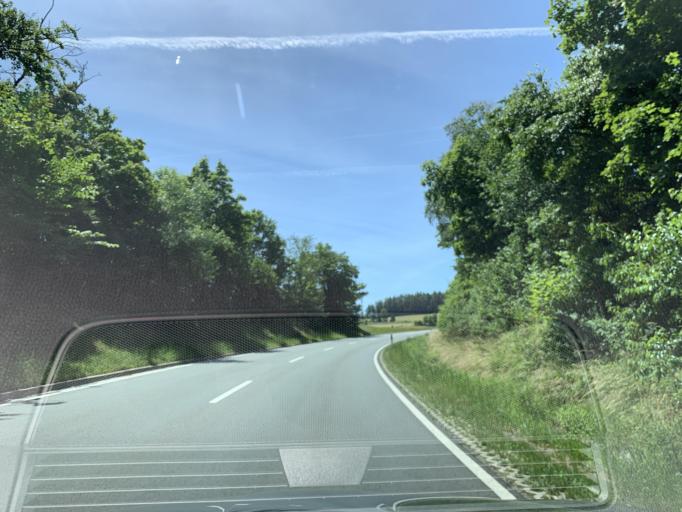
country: DE
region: Bavaria
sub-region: Upper Palatinate
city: Pettendorf
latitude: 49.3438
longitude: 12.3694
